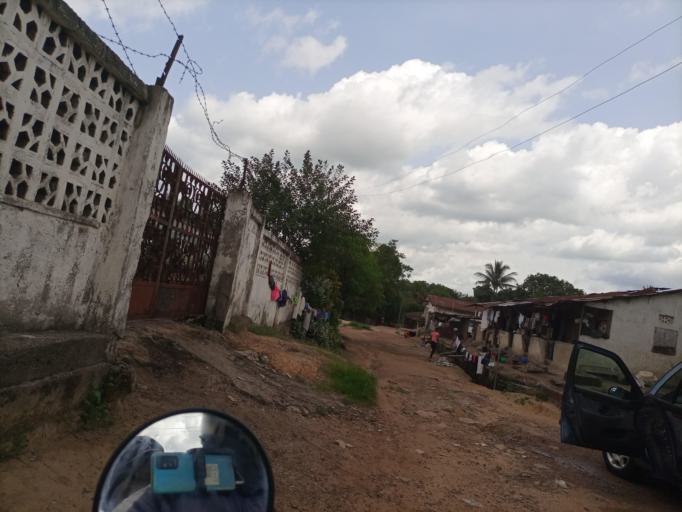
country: SL
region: Southern Province
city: Bo
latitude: 7.9481
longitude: -11.7319
